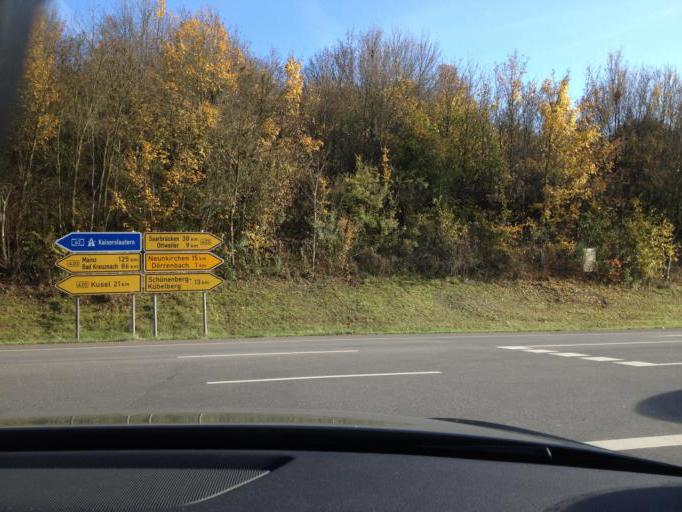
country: DE
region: Rheinland-Pfalz
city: Breitenbach
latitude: 49.4456
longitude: 7.2321
